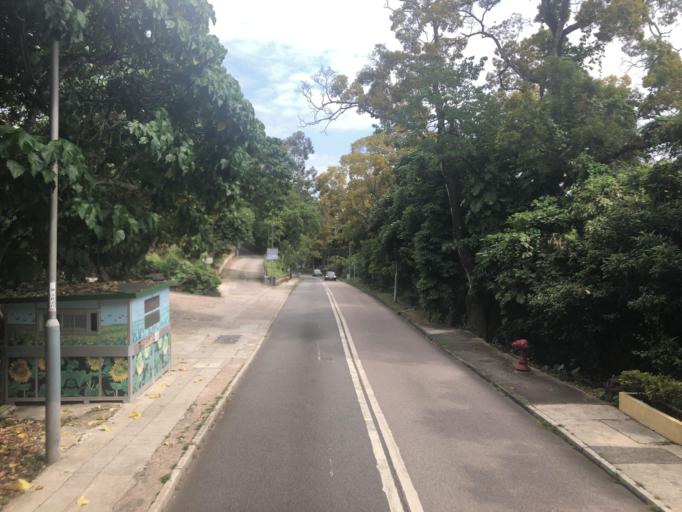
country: HK
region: Sai Kung
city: Sai Kung
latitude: 22.3956
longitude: 114.2871
